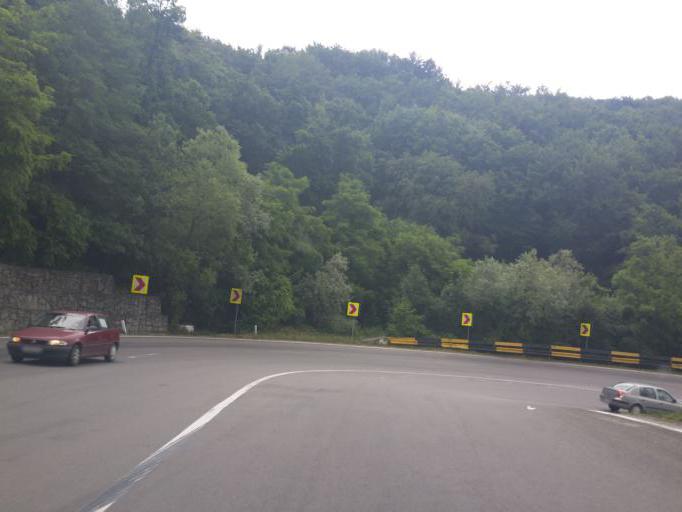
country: RO
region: Salaj
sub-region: Comuna Treznea
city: Treznea
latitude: 47.1526
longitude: 23.0901
